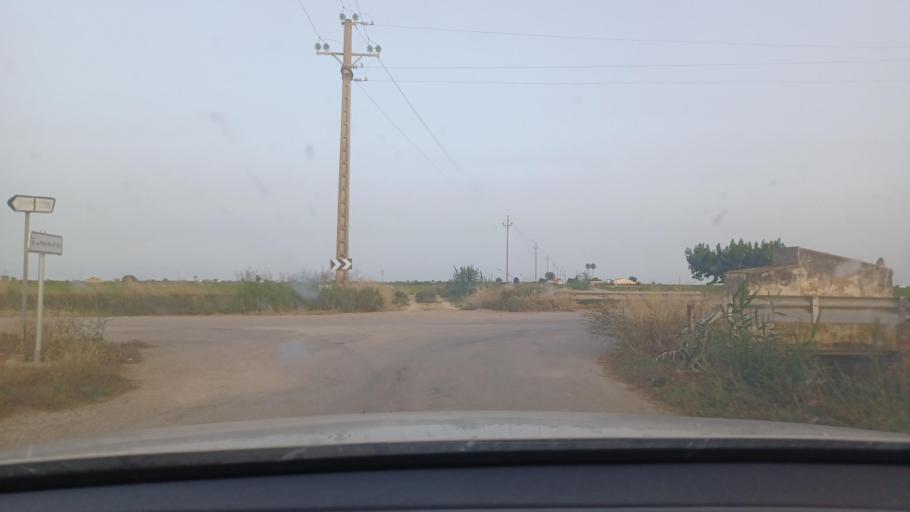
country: ES
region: Catalonia
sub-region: Provincia de Tarragona
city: Deltebre
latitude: 40.6818
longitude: 0.6576
